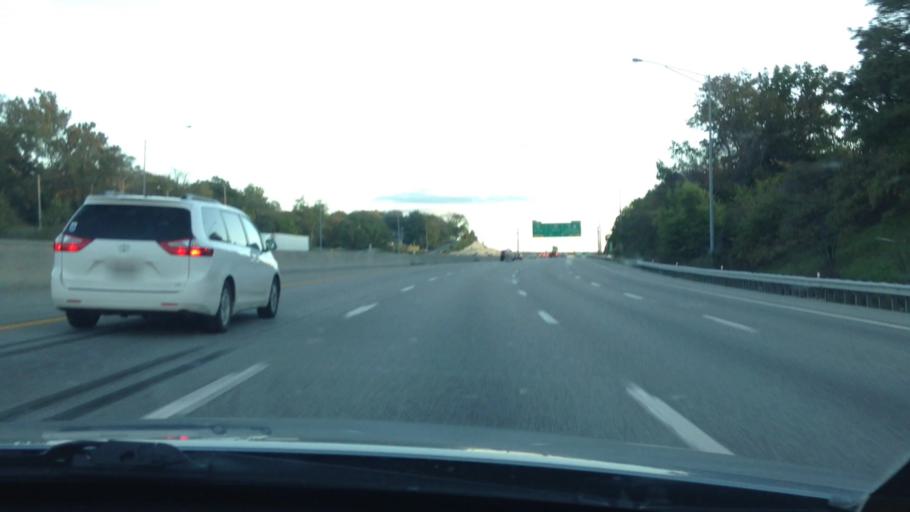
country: US
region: Missouri
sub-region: Jackson County
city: Sugar Creek
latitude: 39.0710
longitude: -94.4881
